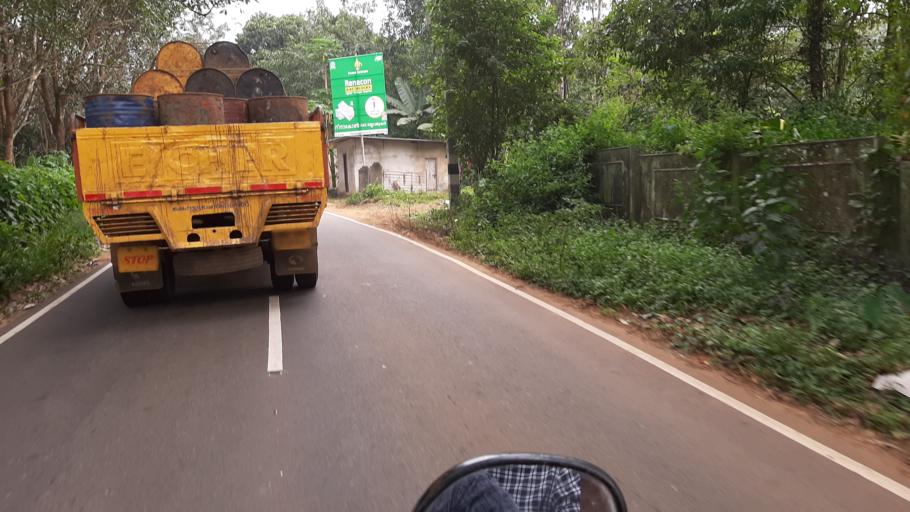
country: IN
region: Kerala
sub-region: Pattanamtitta
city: Pathanamthitta
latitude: 9.4688
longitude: 76.8696
